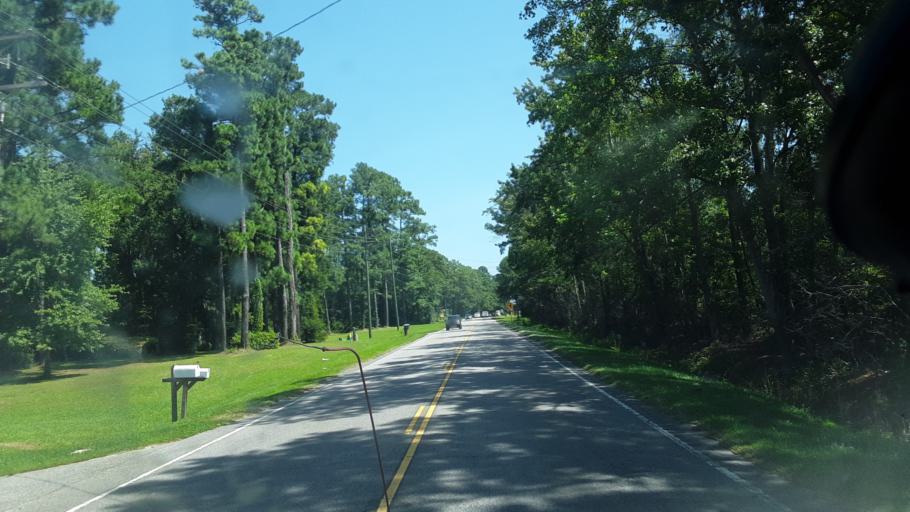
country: US
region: South Carolina
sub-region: Horry County
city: Forestbrook
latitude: 33.8339
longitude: -78.8842
